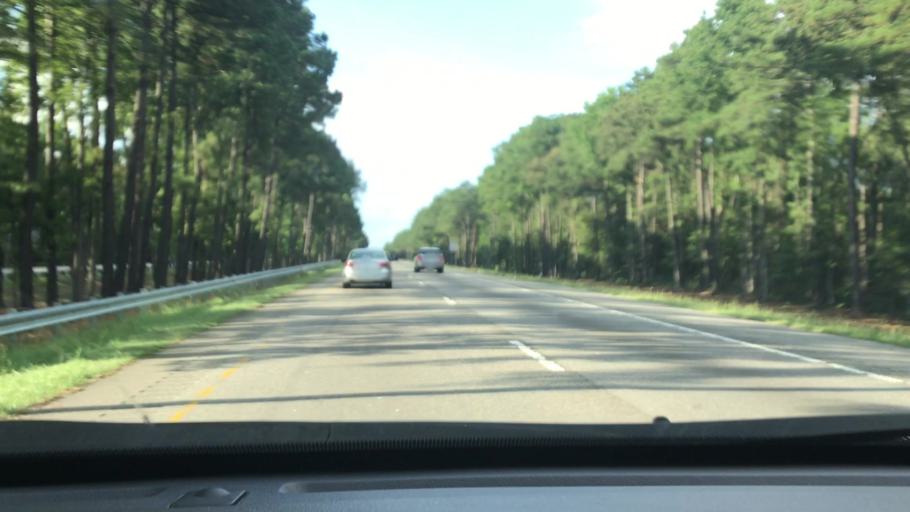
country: US
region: North Carolina
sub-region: Robeson County
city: Lumberton
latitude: 34.6824
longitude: -79.0018
